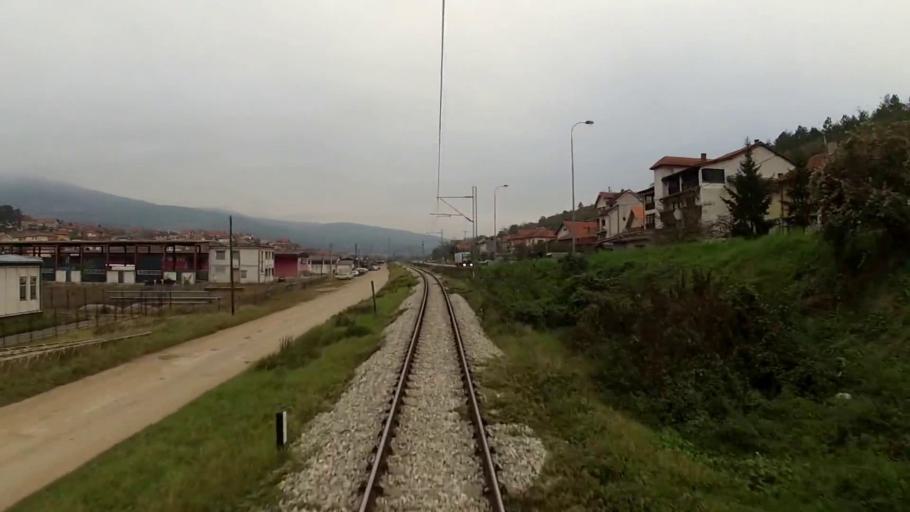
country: RS
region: Central Serbia
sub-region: Pirotski Okrug
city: Dimitrovgrad
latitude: 43.0152
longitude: 22.7929
